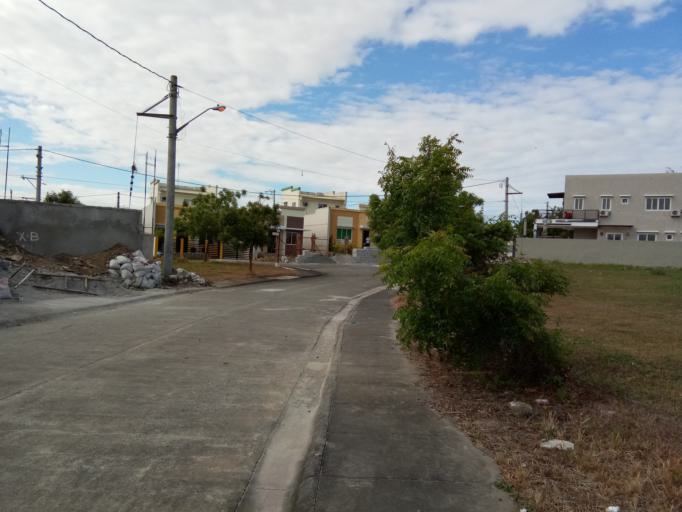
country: PH
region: Calabarzon
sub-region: Province of Cavite
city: Bulihan
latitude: 14.2811
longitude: 120.9729
